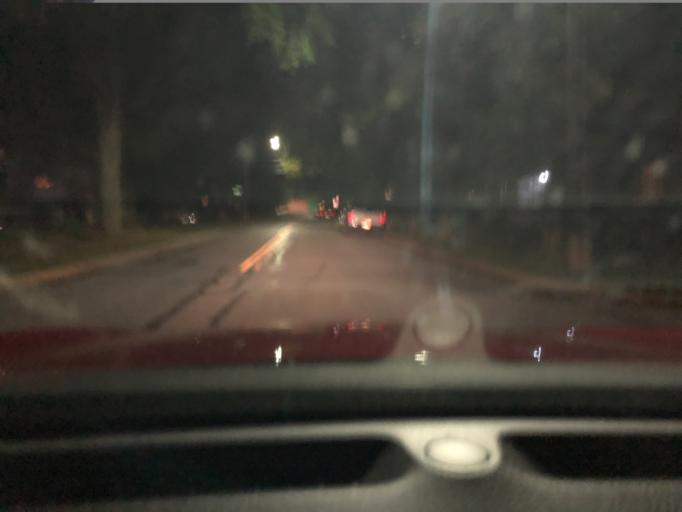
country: US
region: Indiana
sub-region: DeKalb County
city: Auburn
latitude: 41.3612
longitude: -85.0556
